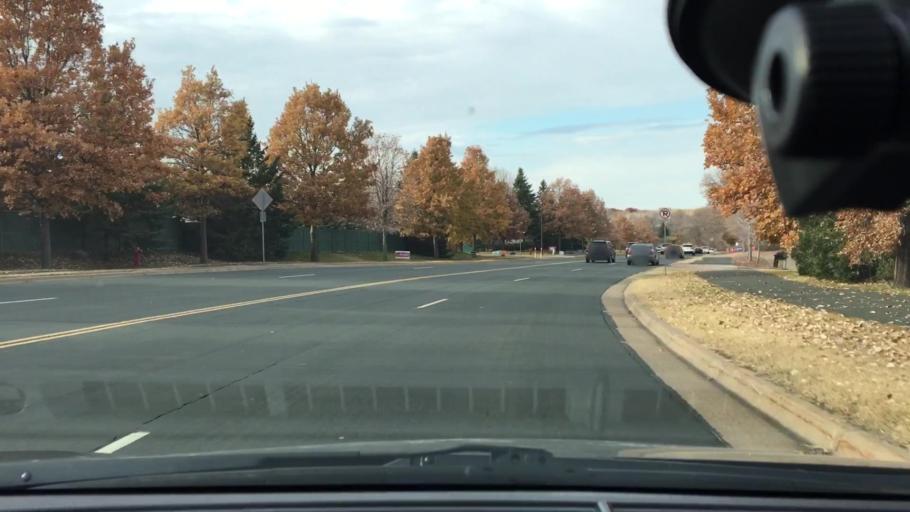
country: US
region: Minnesota
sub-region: Hennepin County
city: Maple Grove
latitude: 45.1034
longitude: -93.4762
